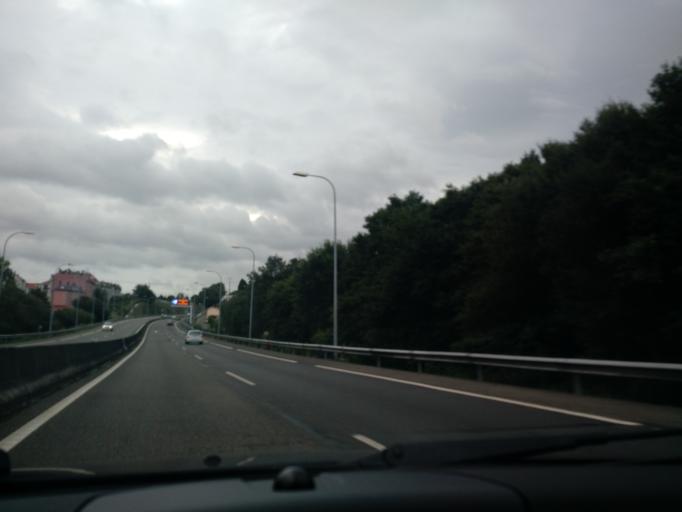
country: ES
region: Galicia
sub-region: Provincia da Coruna
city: Culleredo
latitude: 43.3134
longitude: -8.3743
